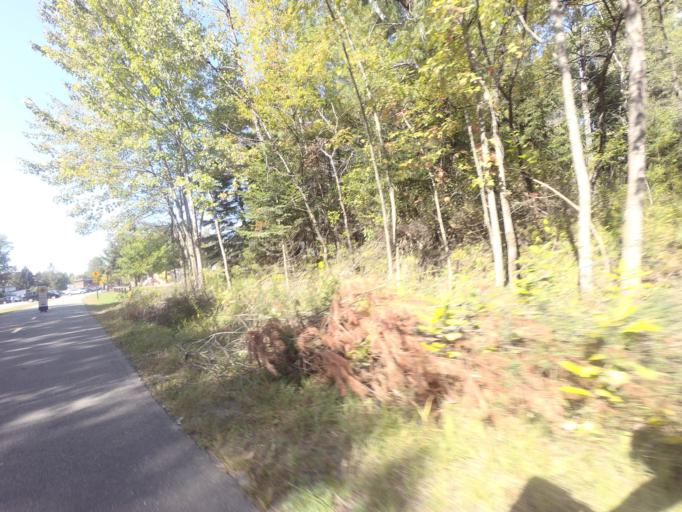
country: CA
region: Quebec
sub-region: Laurentides
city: Mont-Tremblant
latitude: 46.1292
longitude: -74.5886
